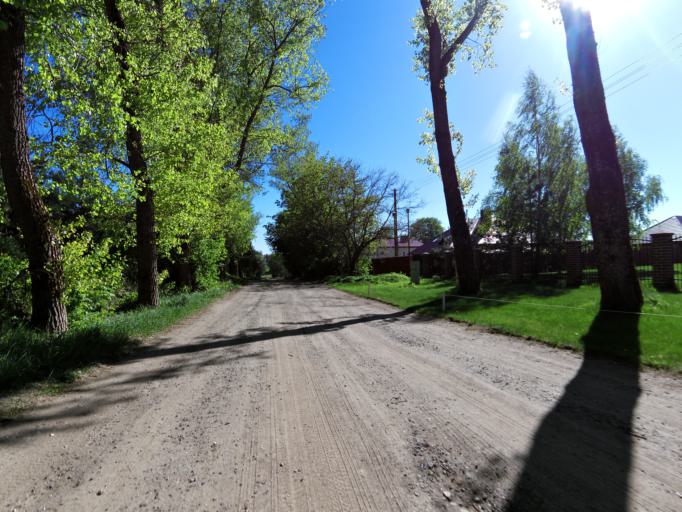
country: LT
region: Vilnius County
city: Pilaite
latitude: 54.6983
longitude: 25.1640
